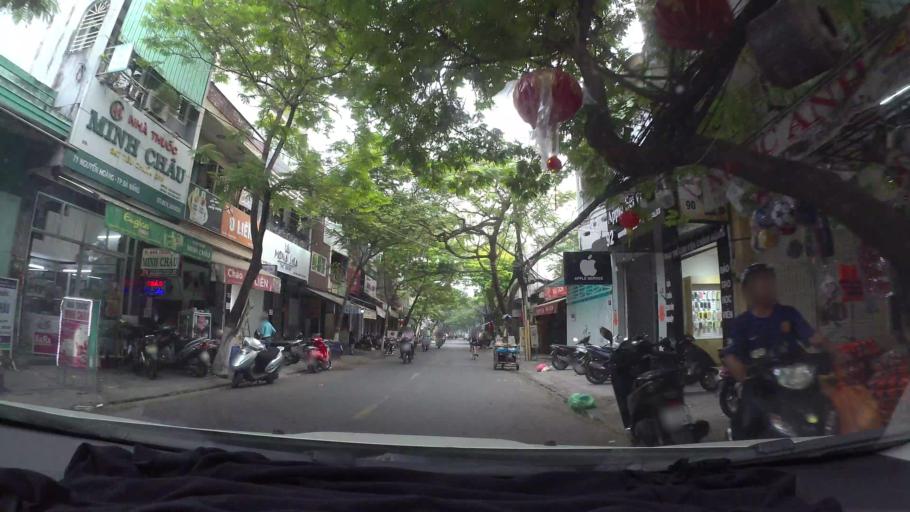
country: VN
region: Da Nang
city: Da Nang
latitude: 16.0633
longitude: 108.2141
